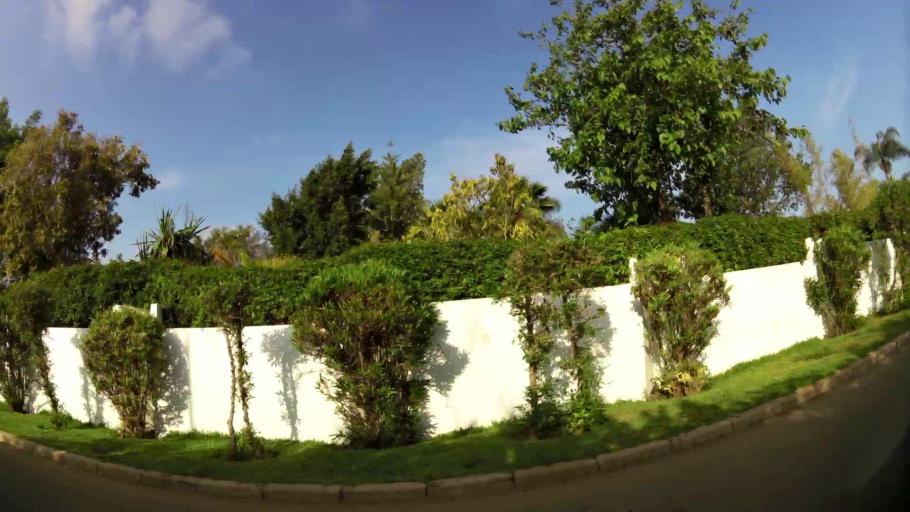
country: MA
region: Rabat-Sale-Zemmour-Zaer
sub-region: Rabat
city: Rabat
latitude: 33.9419
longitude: -6.8120
